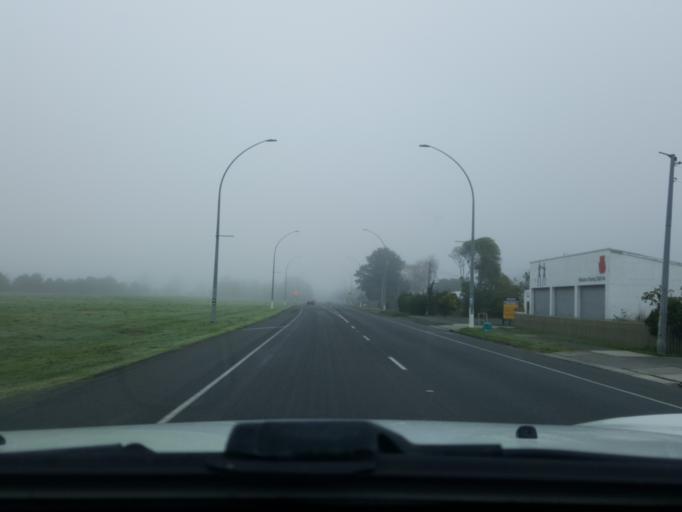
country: NZ
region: Waikato
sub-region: Waikato District
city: Ngaruawahia
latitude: -37.6747
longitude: 175.1577
